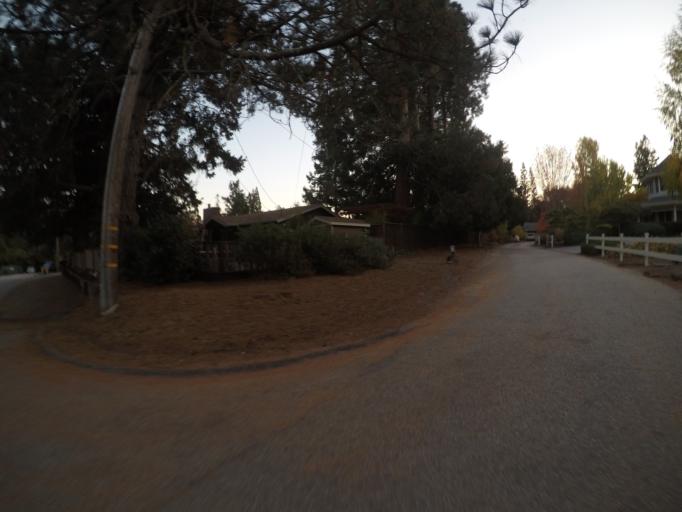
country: US
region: California
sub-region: Santa Cruz County
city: Mount Hermon
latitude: 37.0400
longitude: -122.0423
